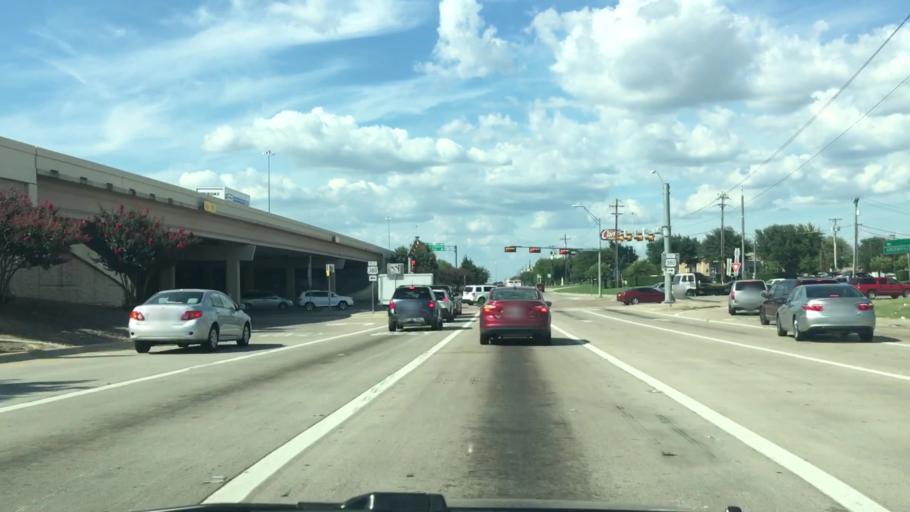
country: US
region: Texas
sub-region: Collin County
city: McKinney
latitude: 33.2161
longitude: -96.6361
